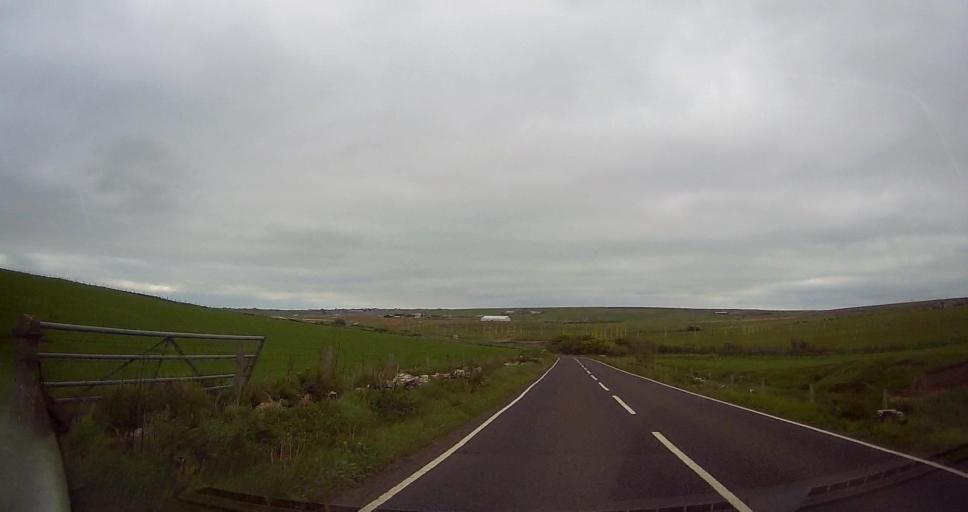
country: GB
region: Scotland
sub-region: Orkney Islands
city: Kirkwall
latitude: 58.9614
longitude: -2.9275
